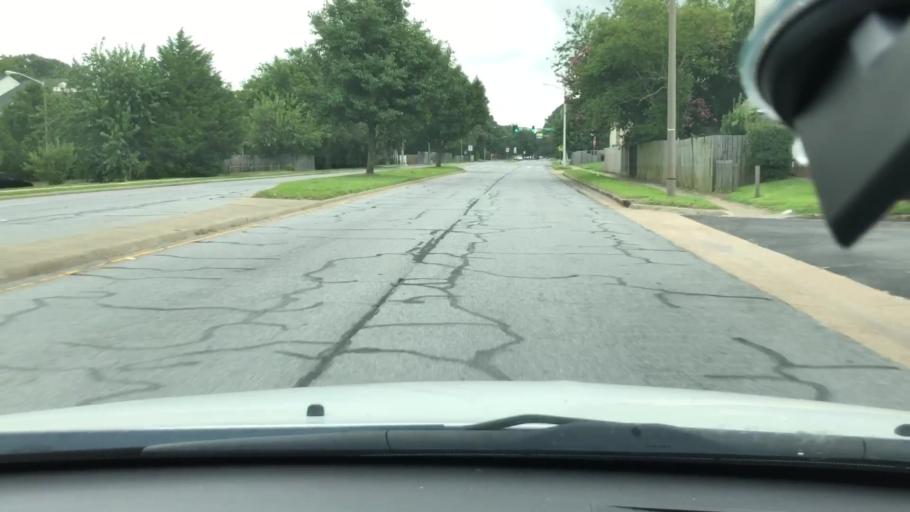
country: US
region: Virginia
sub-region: City of Chesapeake
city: Chesapeake
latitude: 36.8144
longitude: -76.1838
